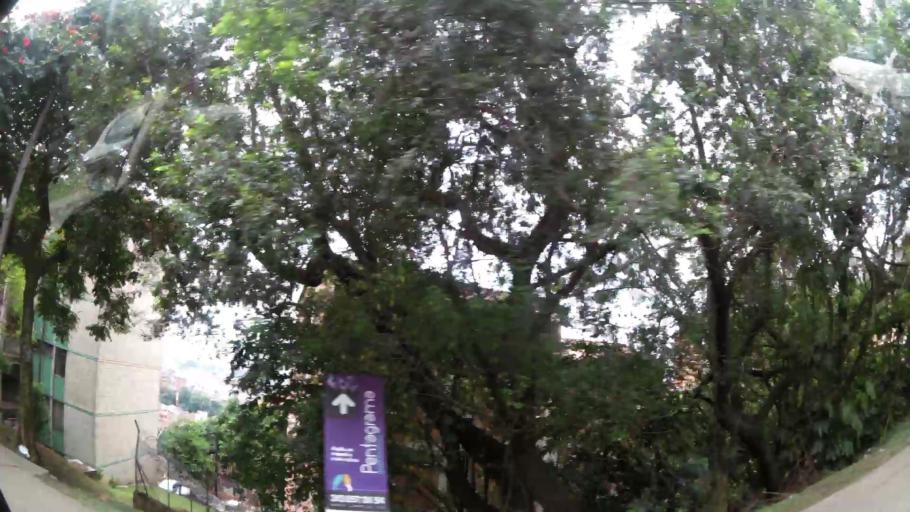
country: CO
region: Antioquia
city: Itagui
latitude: 6.1994
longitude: -75.5922
